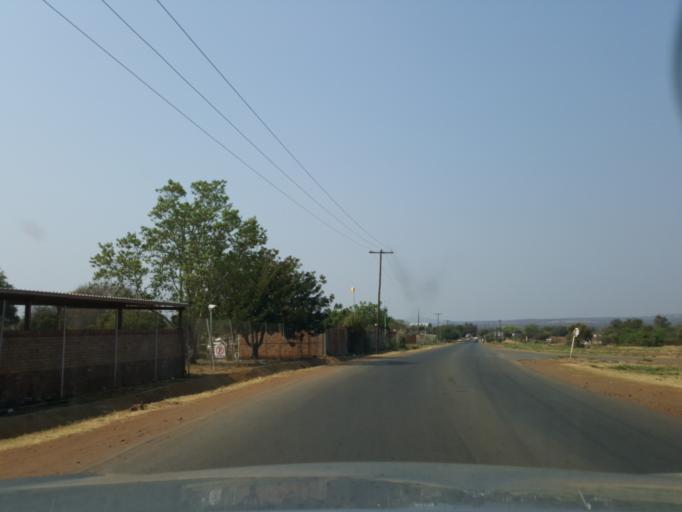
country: ZA
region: North-West
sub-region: Ngaka Modiri Molema District Municipality
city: Zeerust
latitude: -25.4879
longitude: 25.9842
